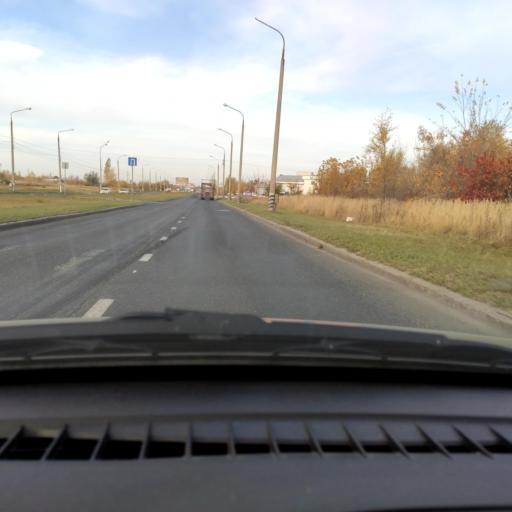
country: RU
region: Samara
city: Tol'yatti
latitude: 53.5572
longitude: 49.3363
